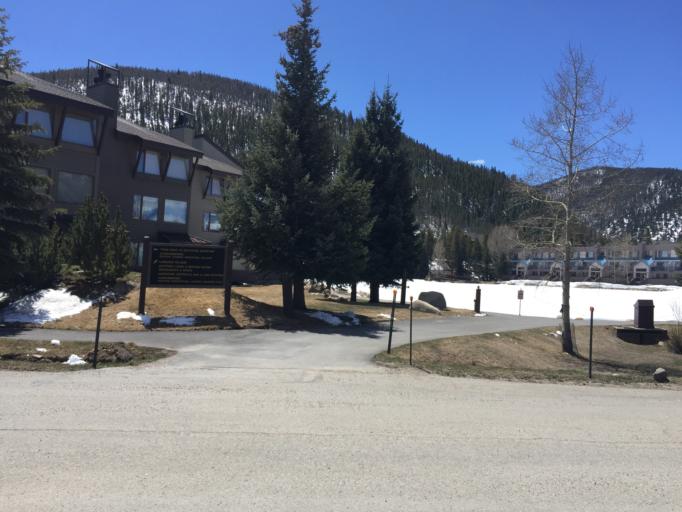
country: US
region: Colorado
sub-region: Summit County
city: Keystone
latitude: 39.6076
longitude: -105.9671
